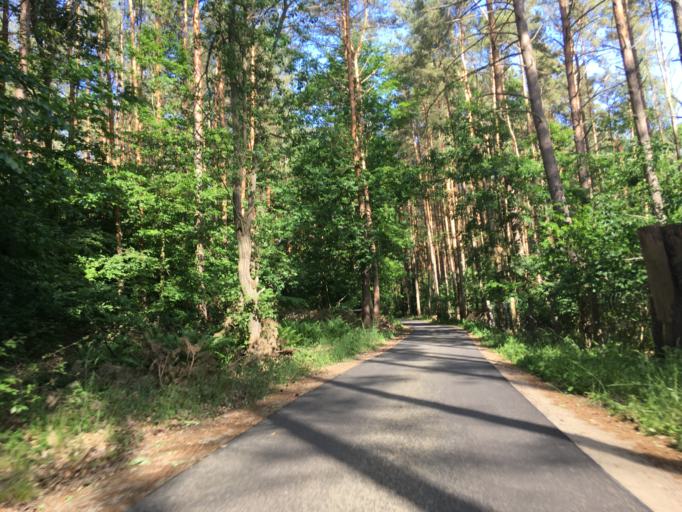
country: DE
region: Brandenburg
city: Althuttendorf
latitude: 52.9907
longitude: 13.7943
